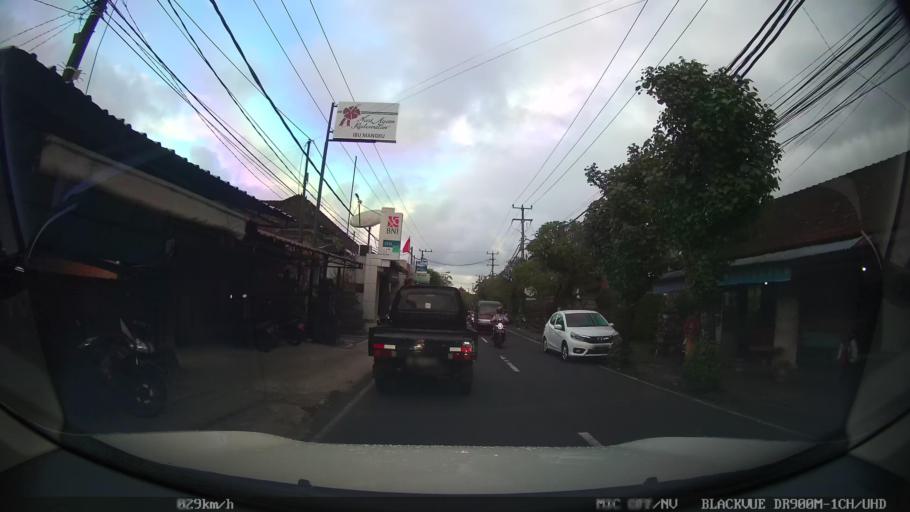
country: ID
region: Bali
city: Bunutan
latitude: -8.4834
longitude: 115.2465
